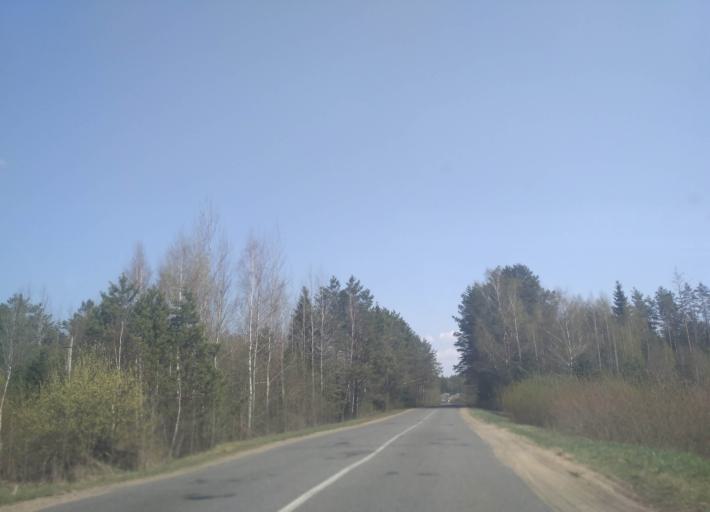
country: BY
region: Minsk
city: Loshnitsa
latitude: 54.4188
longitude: 28.6410
